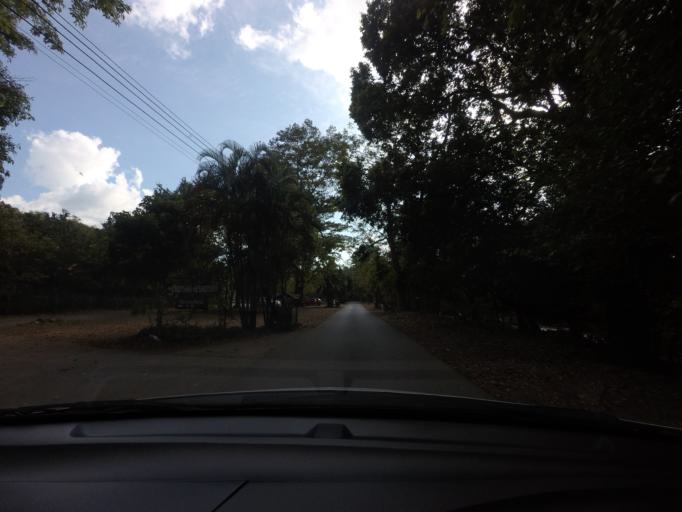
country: TH
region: Nakhon Nayok
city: Nakhon Nayok
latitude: 14.3338
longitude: 101.3059
